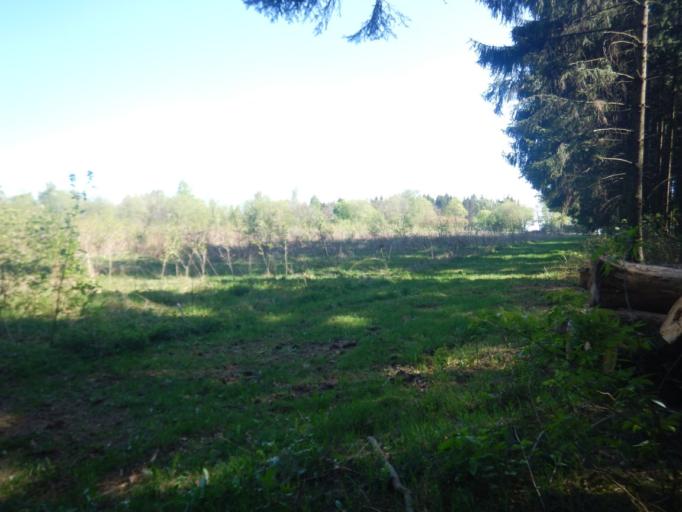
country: LU
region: Diekirch
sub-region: Canton de Clervaux
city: Troisvierges
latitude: 50.1593
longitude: 6.0296
